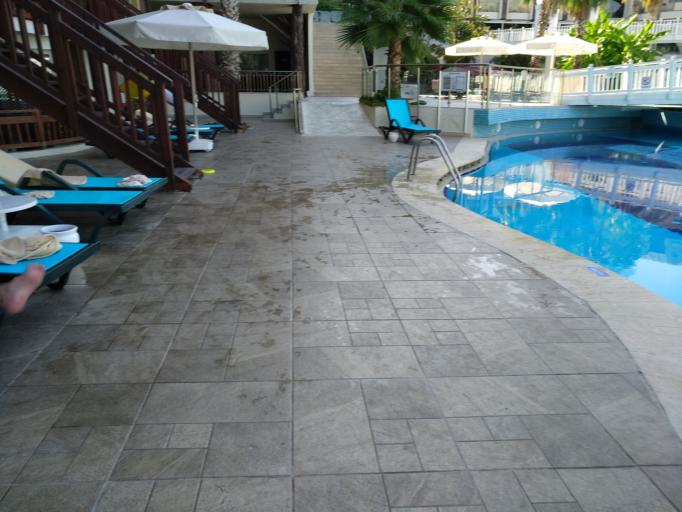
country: TR
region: Antalya
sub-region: Kemer
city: Goeynuek
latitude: 36.6649
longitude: 30.5594
